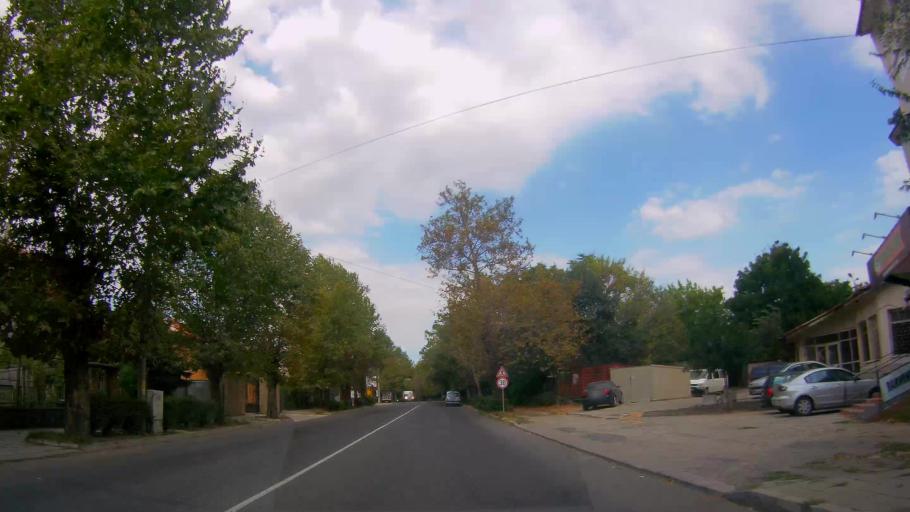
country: BG
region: Burgas
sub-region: Obshtina Aytos
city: Aytos
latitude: 42.7006
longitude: 27.2476
